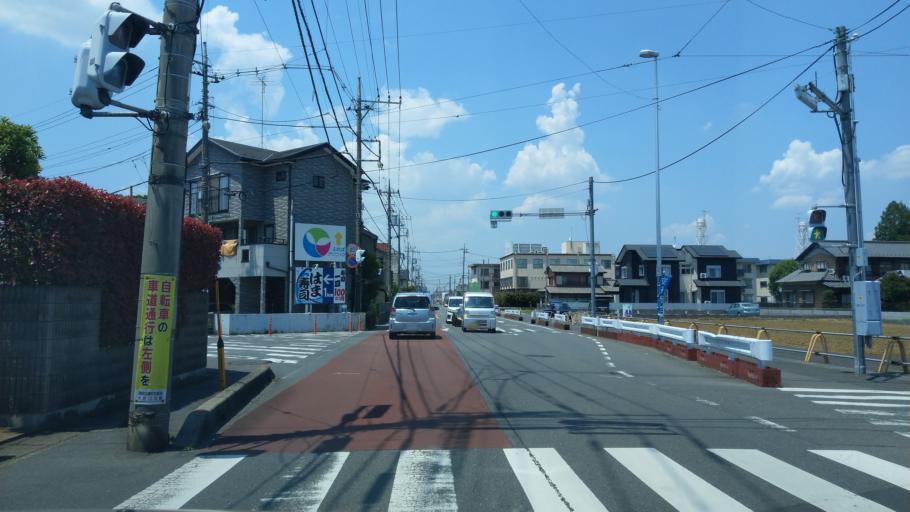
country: JP
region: Saitama
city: Saitama
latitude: 35.8664
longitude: 139.6817
